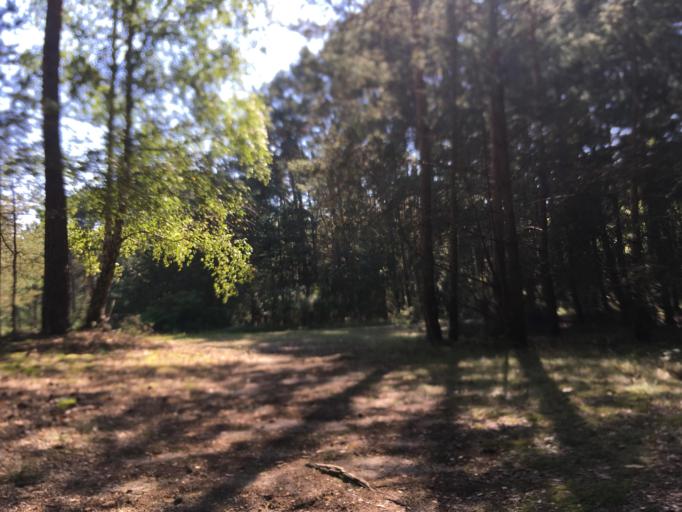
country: DE
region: Brandenburg
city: Gross Koris
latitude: 52.1993
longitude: 13.7392
